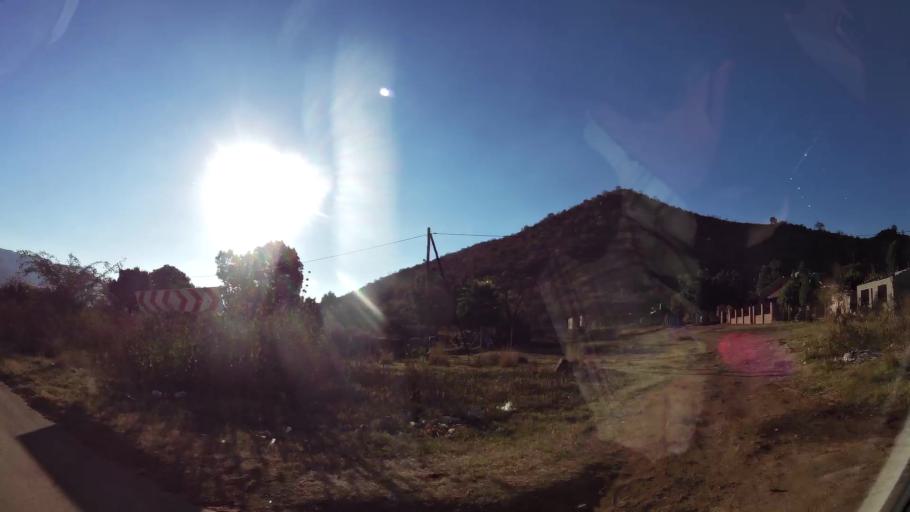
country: ZA
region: Limpopo
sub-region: Waterberg District Municipality
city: Mokopane
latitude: -24.1637
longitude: 28.9736
